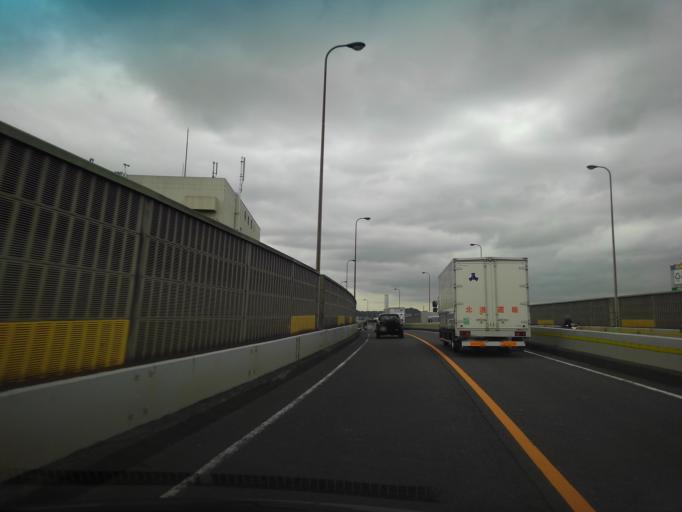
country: JP
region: Tokyo
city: Hachioji
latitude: 35.6633
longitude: 139.3531
